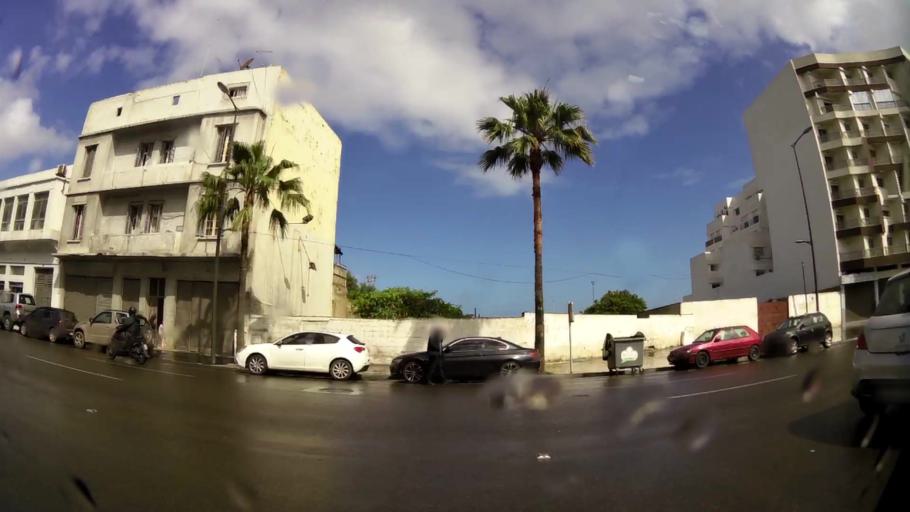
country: MA
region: Grand Casablanca
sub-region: Casablanca
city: Casablanca
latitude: 33.6009
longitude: -7.5867
